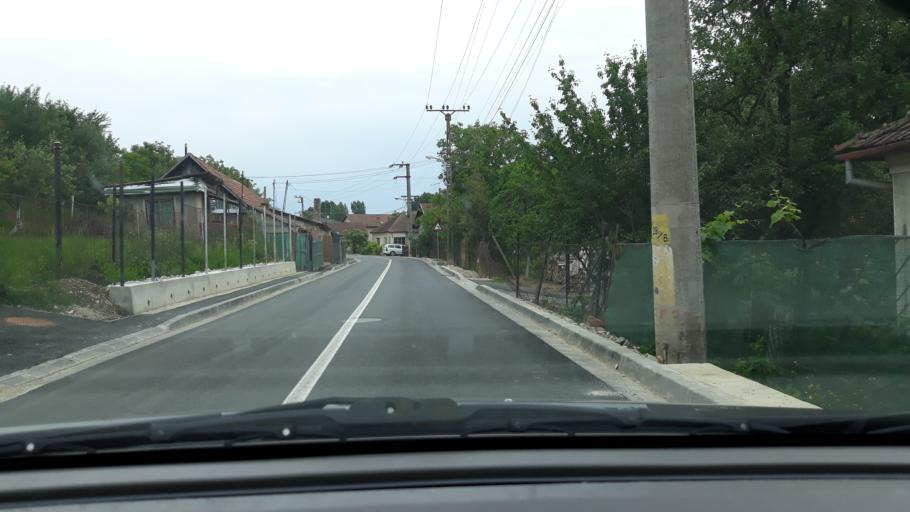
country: RO
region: Bihor
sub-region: Comuna Osorheiu
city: Alparea
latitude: 47.0593
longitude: 22.0079
